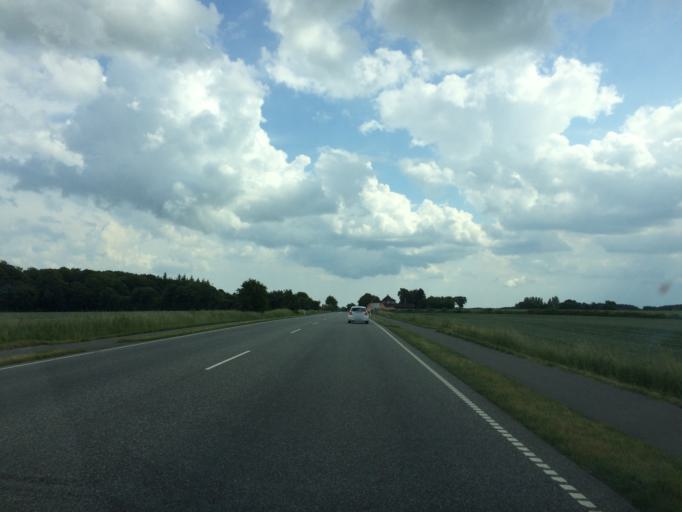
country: DK
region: South Denmark
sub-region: Vejle Kommune
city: Borkop
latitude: 55.6190
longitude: 9.6112
